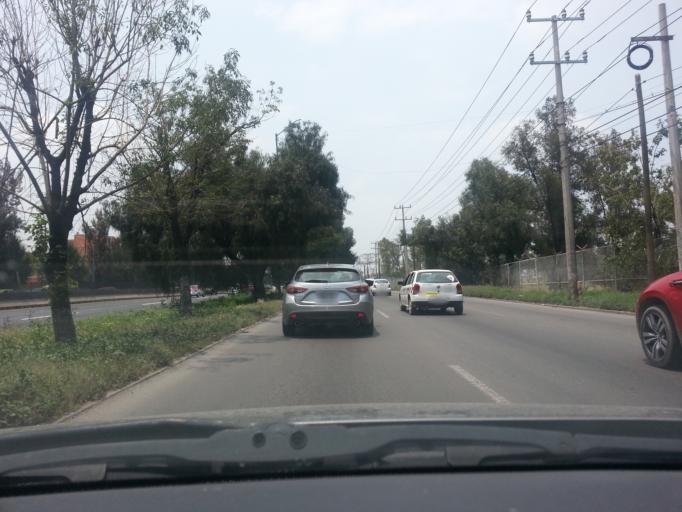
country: MX
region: Mexico
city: Cuautitlan Izcalli
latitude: 19.6403
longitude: -99.1949
